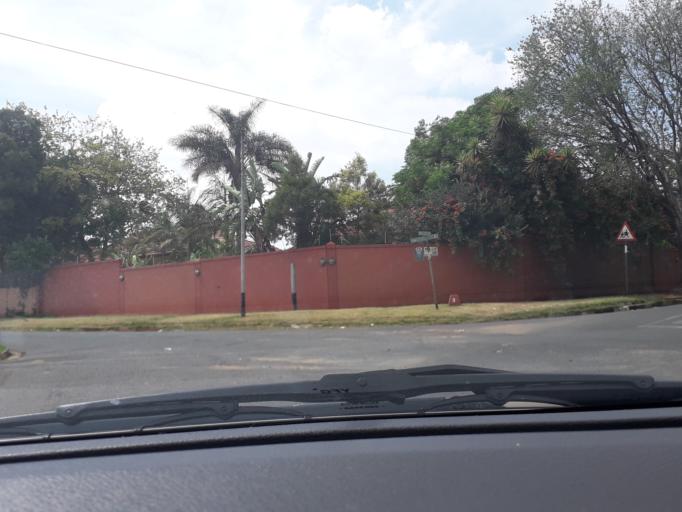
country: ZA
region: Gauteng
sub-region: City of Johannesburg Metropolitan Municipality
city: Johannesburg
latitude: -26.1353
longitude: 28.0849
